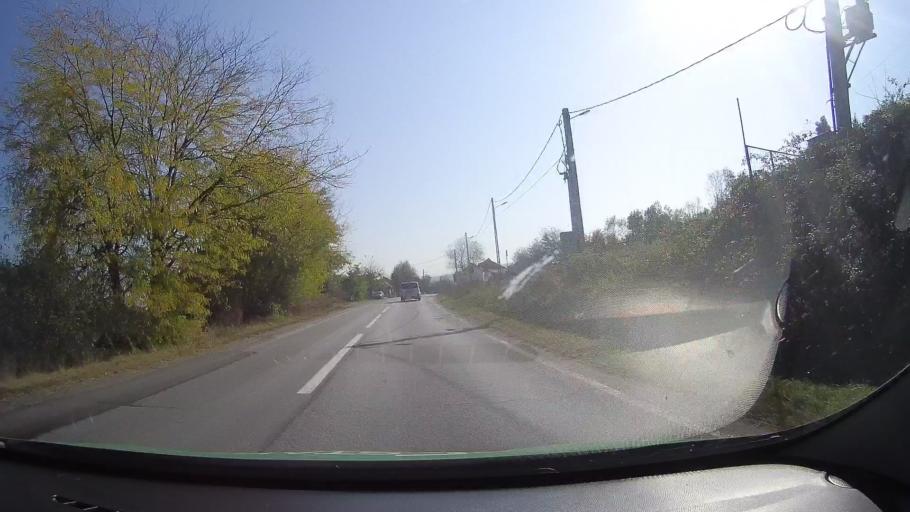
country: RO
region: Hunedoara
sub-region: Comuna Dobra
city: Dobra
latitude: 45.9185
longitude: 22.5571
